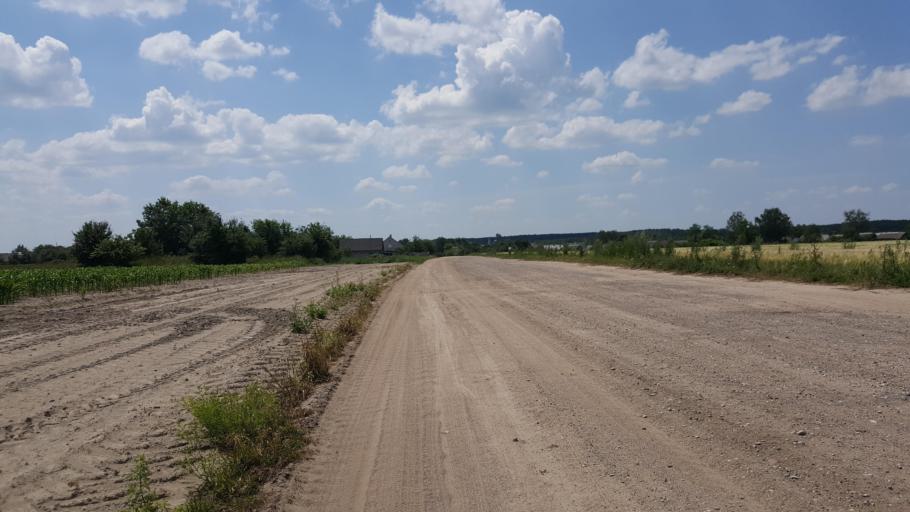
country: BY
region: Brest
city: Kamyanyets
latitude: 52.4000
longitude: 23.7619
